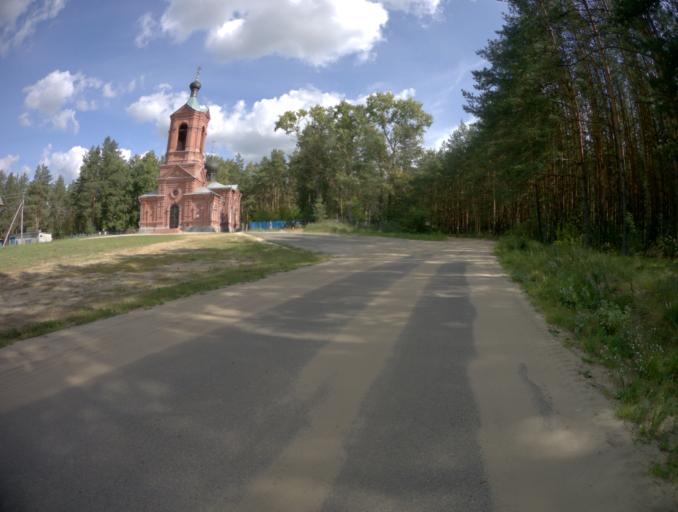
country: RU
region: Vladimir
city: Pokrov
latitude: 55.8645
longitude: 39.3068
